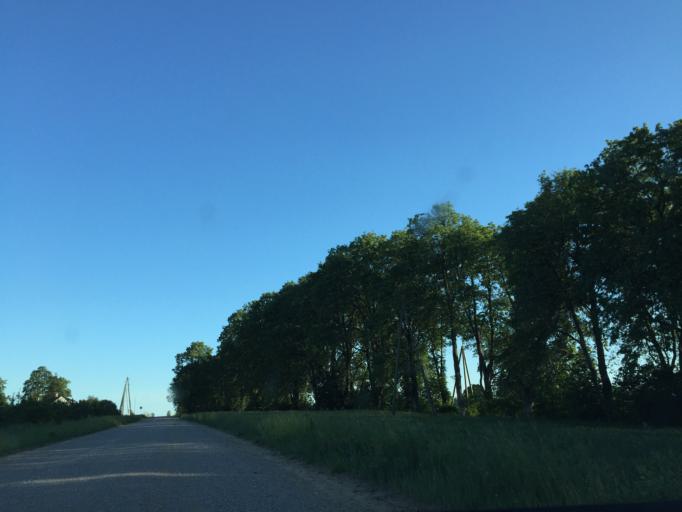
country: LV
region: Broceni
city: Broceni
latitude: 56.8215
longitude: 22.5466
